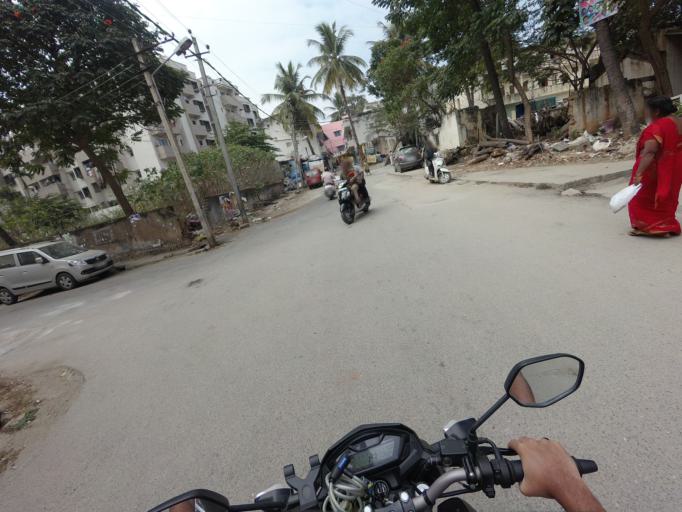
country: IN
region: Karnataka
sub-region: Bangalore Urban
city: Bangalore
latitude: 12.9686
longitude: 77.5406
